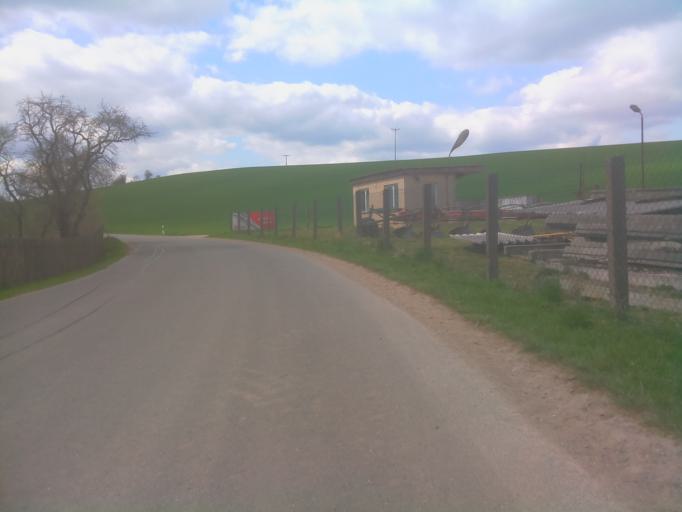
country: DE
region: Thuringia
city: Gneus
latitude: 50.8363
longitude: 11.6746
